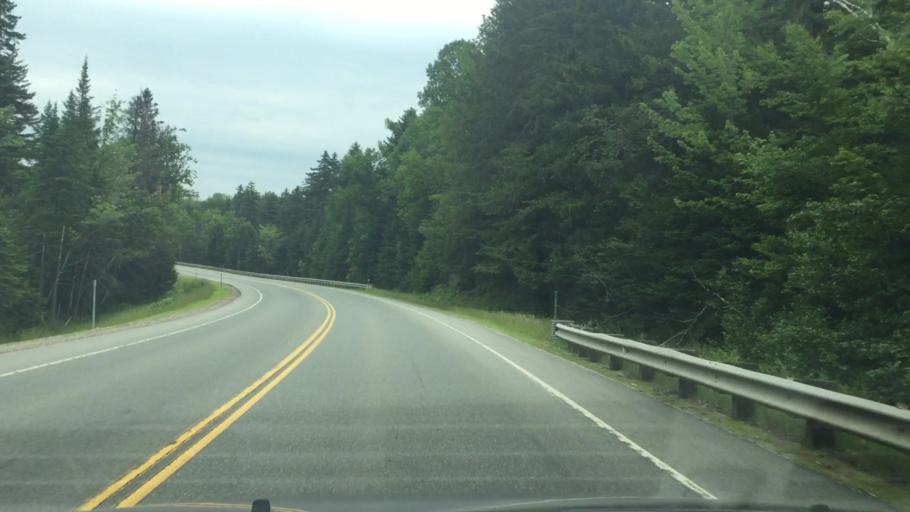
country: US
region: New Hampshire
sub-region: Grafton County
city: Deerfield
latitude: 44.2514
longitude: -71.5931
